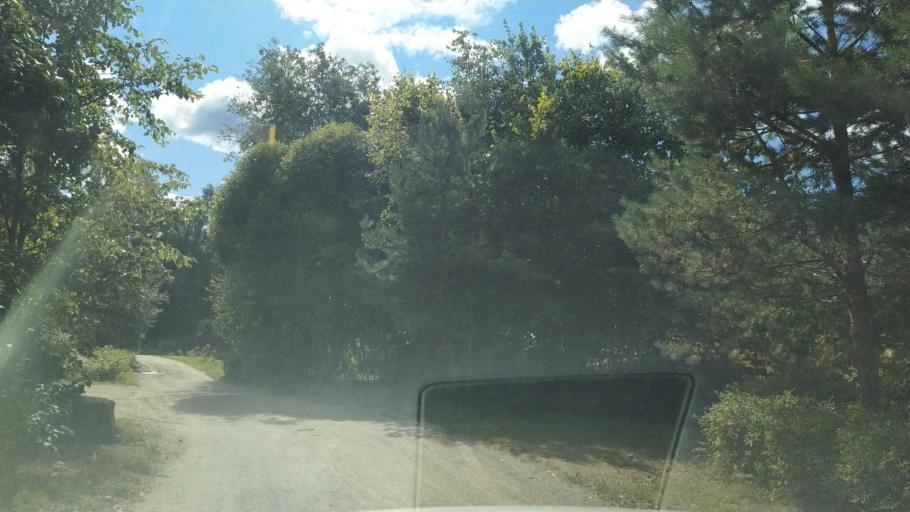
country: RU
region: Leningrad
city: Priozersk
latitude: 60.9986
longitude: 30.1706
